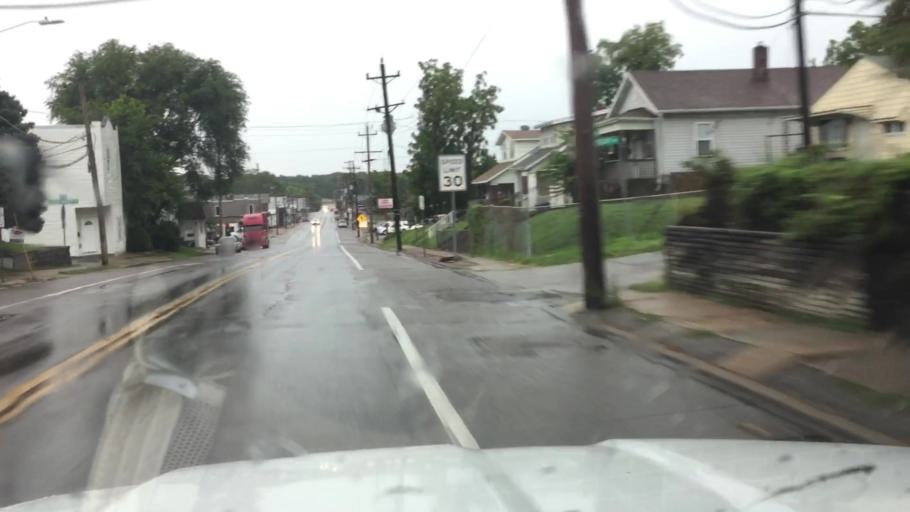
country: US
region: Missouri
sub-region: Saint Louis County
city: Lemay
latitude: 38.5317
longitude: -90.2771
